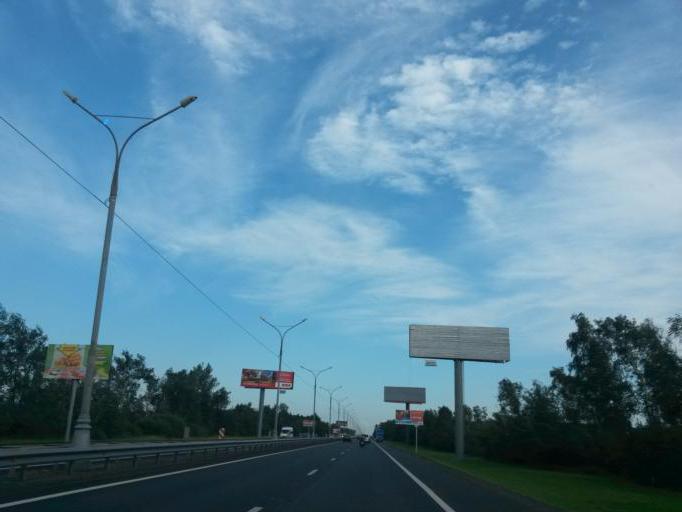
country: RU
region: Moskovskaya
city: Petrovskaya
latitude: 55.5235
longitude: 37.8202
